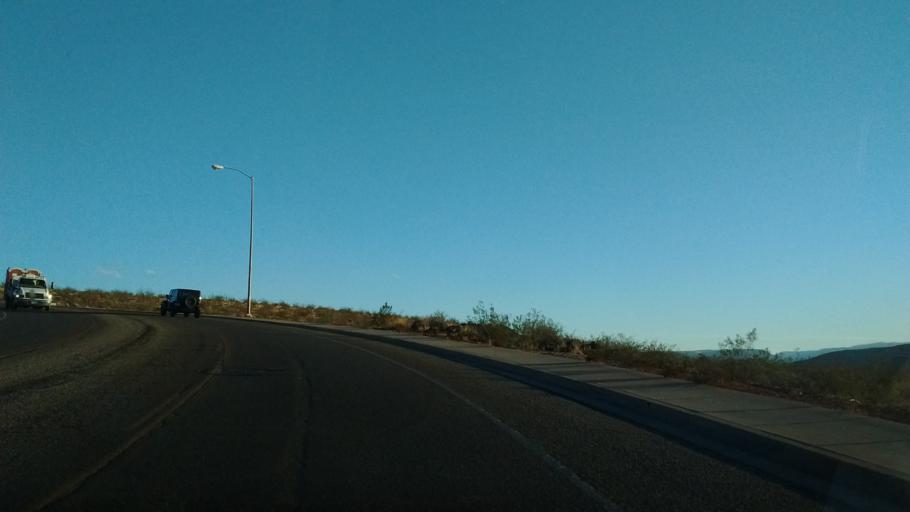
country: US
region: Utah
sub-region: Washington County
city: Saint George
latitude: 37.0935
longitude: -113.5504
